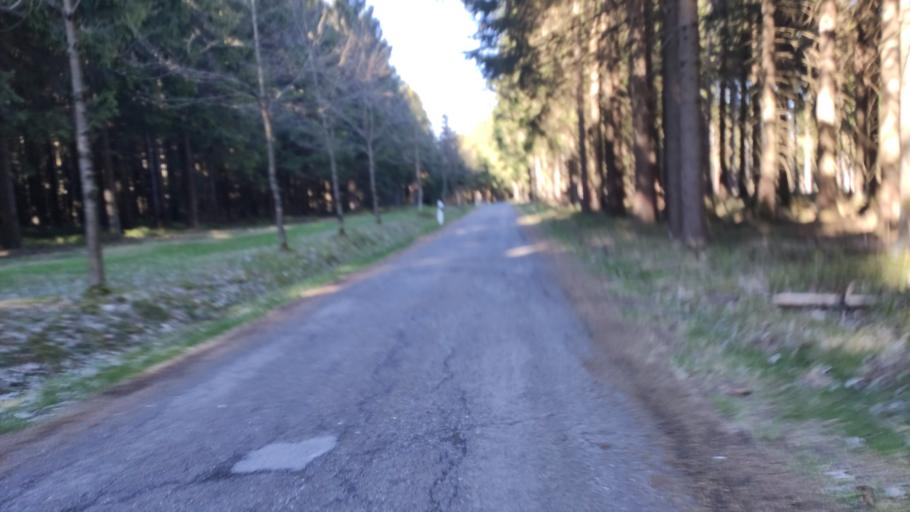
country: DE
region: Bavaria
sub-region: Upper Franconia
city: Tschirn
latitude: 50.4537
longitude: 11.4594
